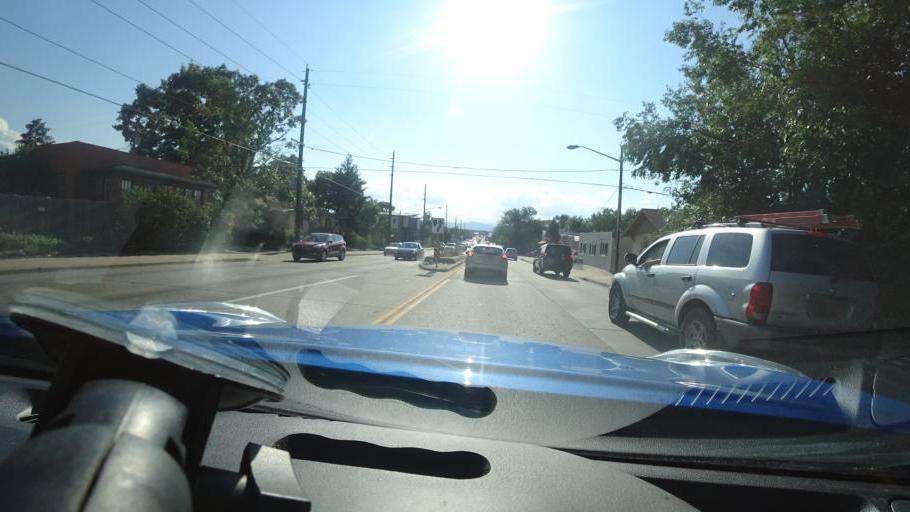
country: US
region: Colorado
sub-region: Arapahoe County
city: Englewood
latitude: 39.6786
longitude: -104.9831
